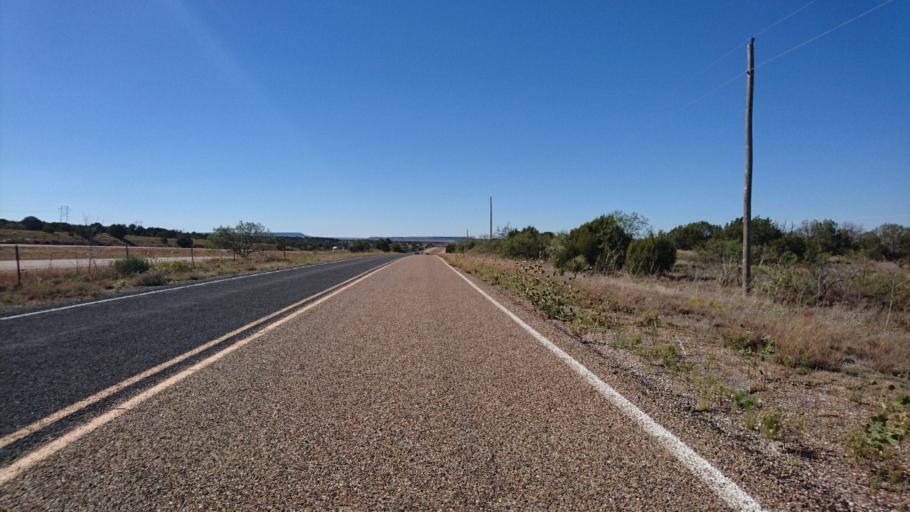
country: US
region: New Mexico
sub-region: Quay County
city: Tucumcari
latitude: 35.0667
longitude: -104.1859
